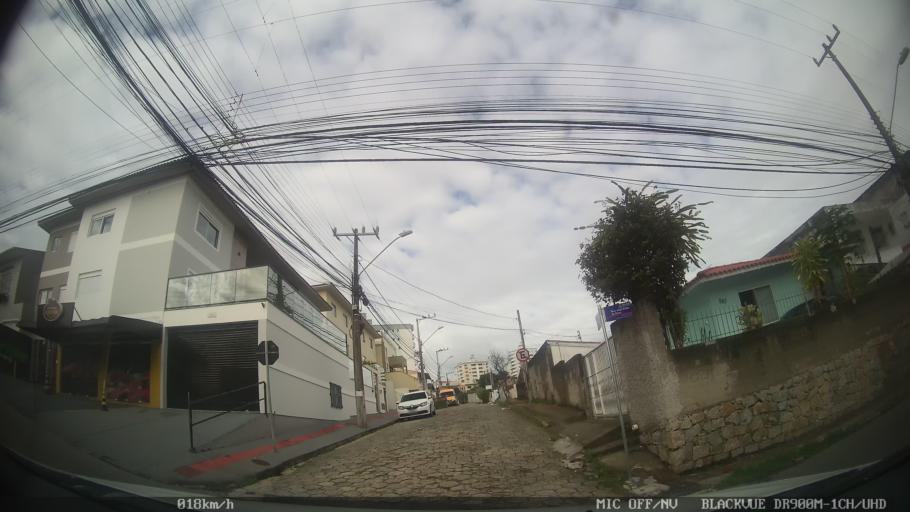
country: BR
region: Santa Catarina
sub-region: Sao Jose
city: Campinas
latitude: -27.5763
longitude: -48.6093
